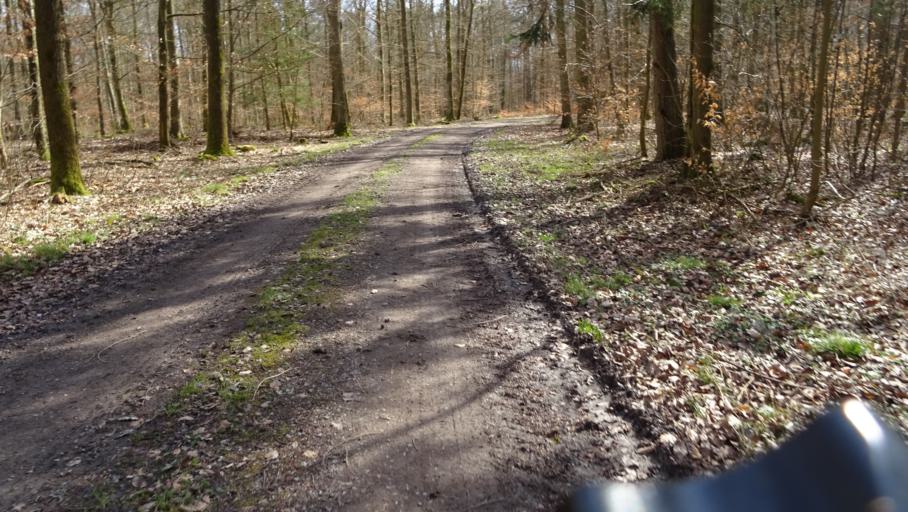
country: DE
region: Baden-Wuerttemberg
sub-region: Karlsruhe Region
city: Seckach
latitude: 49.4073
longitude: 9.3191
